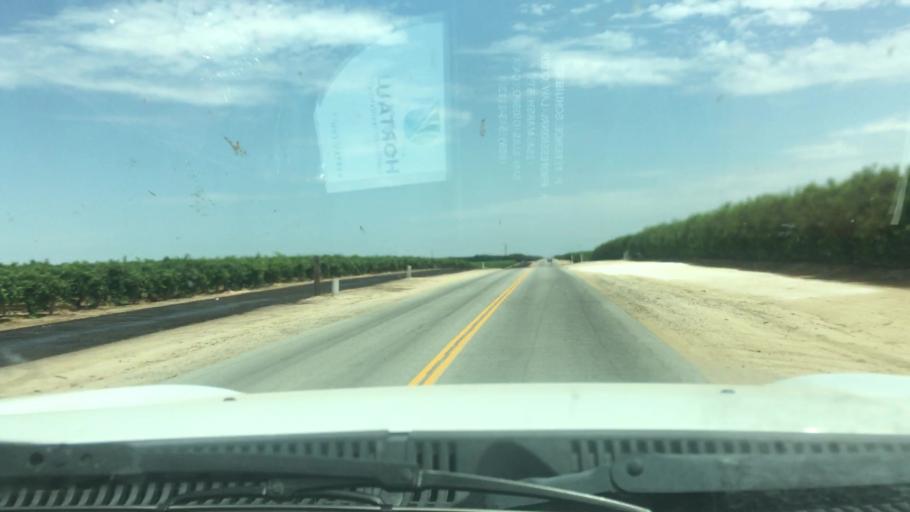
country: US
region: California
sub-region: Kern County
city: McFarland
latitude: 35.5684
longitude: -119.1511
